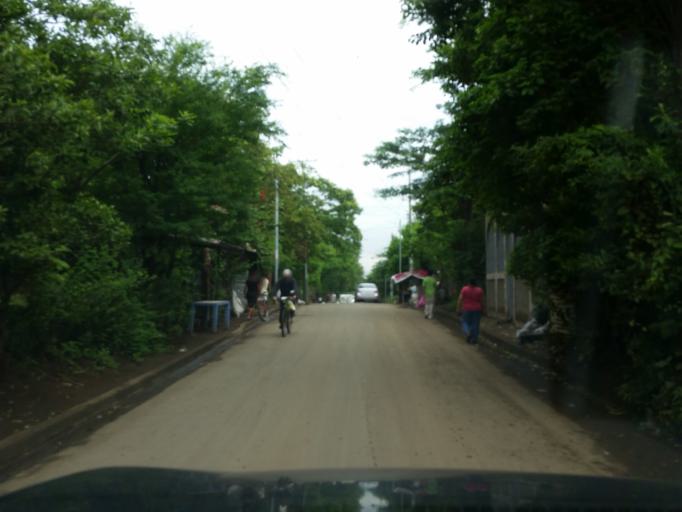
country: NI
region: Managua
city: Managua
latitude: 12.1030
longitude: -86.2190
